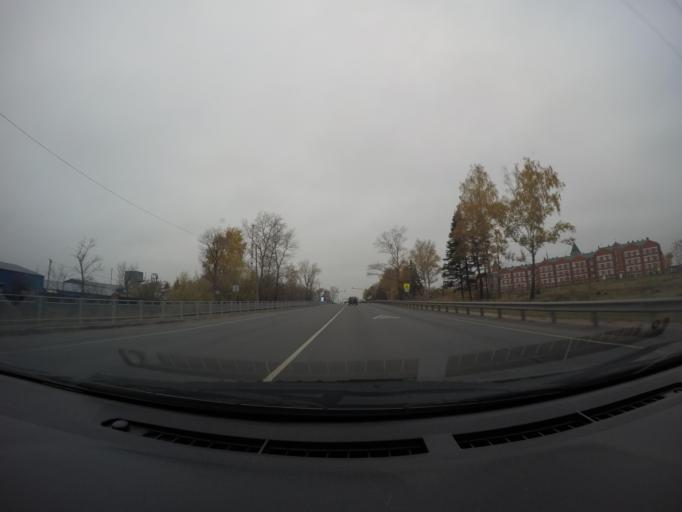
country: RU
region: Moskovskaya
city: Bronnitsy
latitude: 55.4151
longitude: 38.2555
